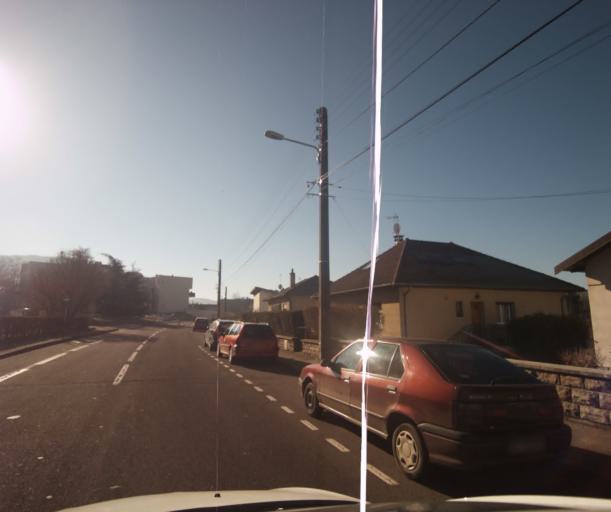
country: FR
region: Franche-Comte
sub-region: Departement du Doubs
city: Besancon
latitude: 47.2338
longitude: 5.9939
